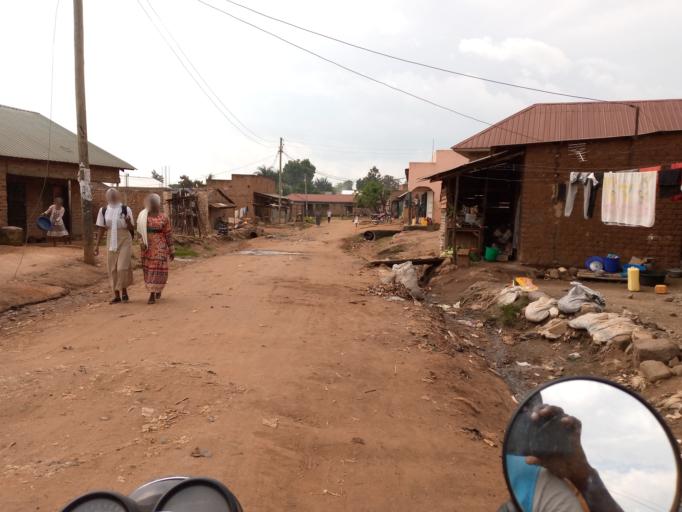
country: UG
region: Eastern Region
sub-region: Mbale District
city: Mbale
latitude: 1.0830
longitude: 34.1648
